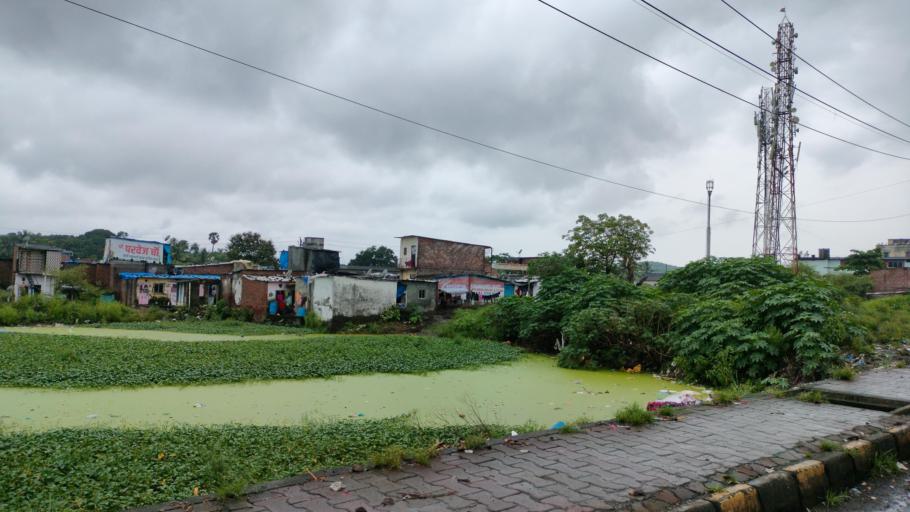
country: IN
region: Maharashtra
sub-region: Thane
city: Virar
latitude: 19.4279
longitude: 72.8428
